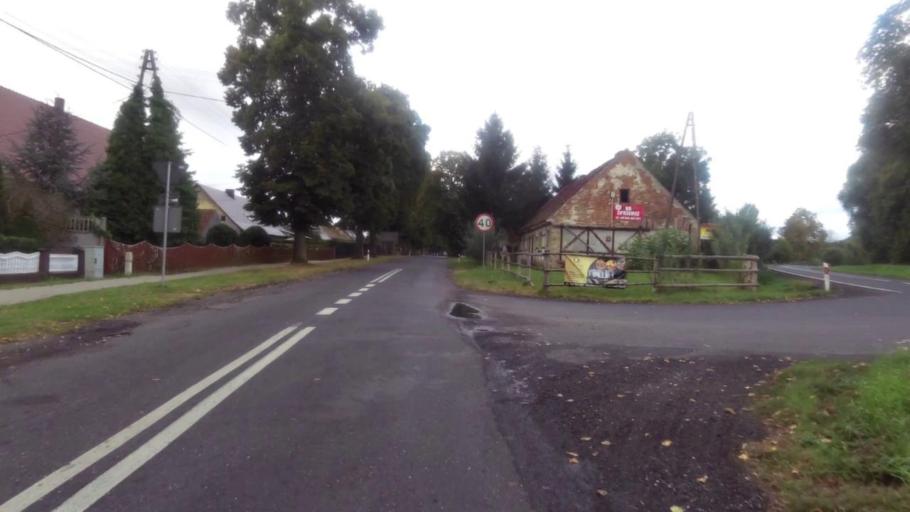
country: PL
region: West Pomeranian Voivodeship
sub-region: Powiat mysliborski
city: Boleszkowice
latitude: 52.6870
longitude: 14.6365
